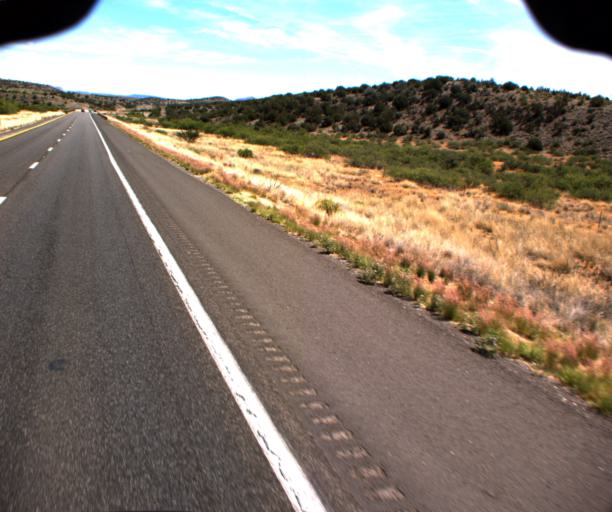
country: US
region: Arizona
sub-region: Yavapai County
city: Cornville
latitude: 34.7801
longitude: -111.9267
